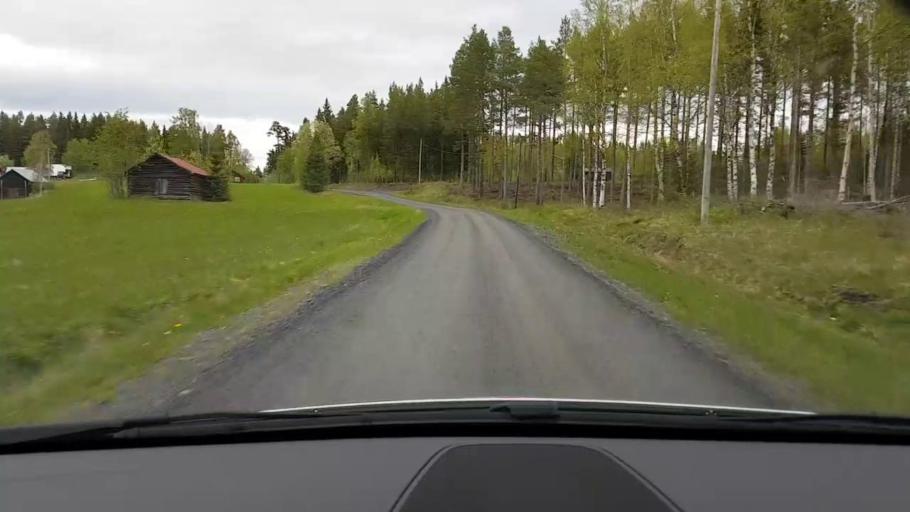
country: SE
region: Jaemtland
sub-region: Krokoms Kommun
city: Krokom
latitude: 63.2934
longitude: 14.3915
